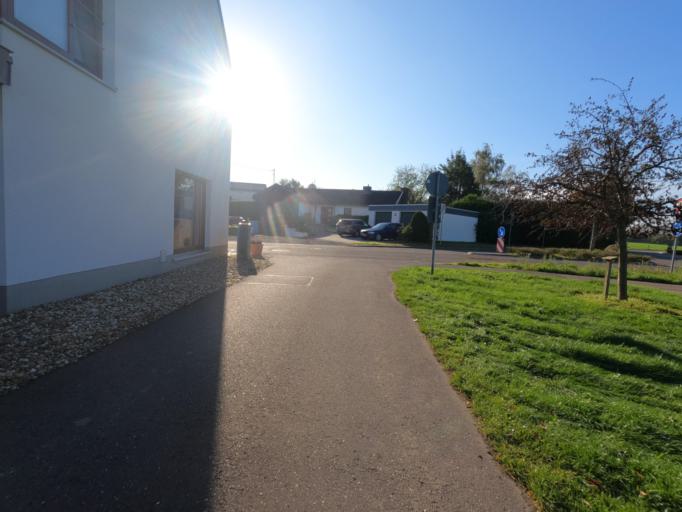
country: DE
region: North Rhine-Westphalia
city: Erkelenz
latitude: 51.0902
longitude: 6.3380
